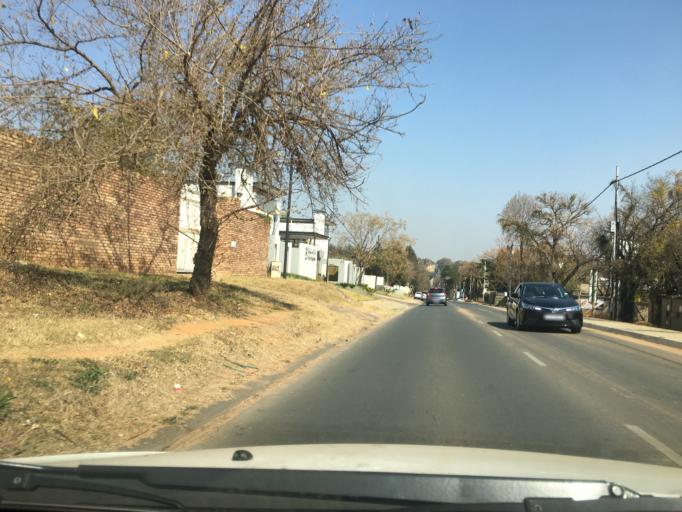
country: ZA
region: Gauteng
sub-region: City of Johannesburg Metropolitan Municipality
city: Midrand
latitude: -26.0631
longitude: 28.0546
